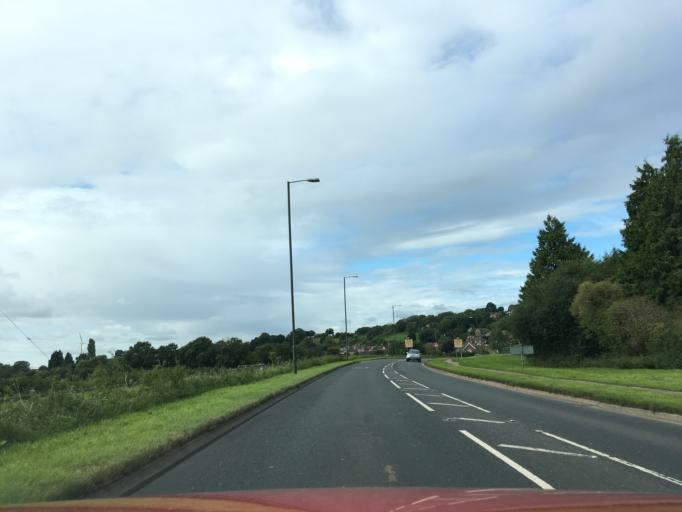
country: GB
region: England
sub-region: Gloucestershire
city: Lydney
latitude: 51.7158
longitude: -2.5477
